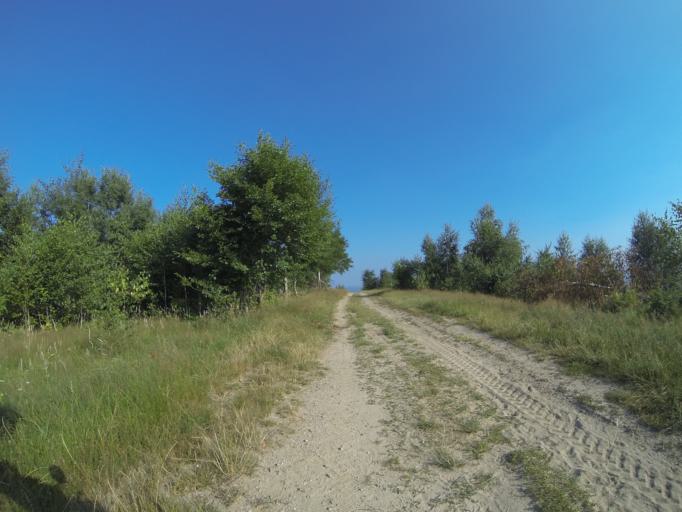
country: RO
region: Valcea
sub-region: Comuna Vaideeni
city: Vaideeni
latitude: 45.2012
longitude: 23.9794
